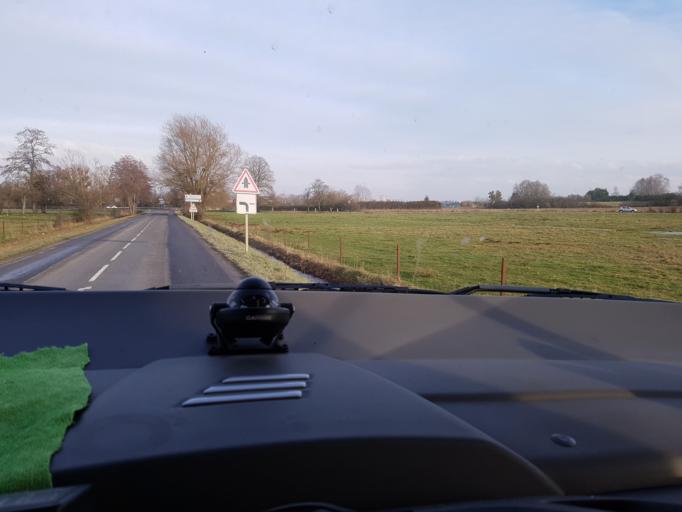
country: FR
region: Champagne-Ardenne
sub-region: Departement des Ardennes
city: Warcq
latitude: 49.7652
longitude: 4.6697
